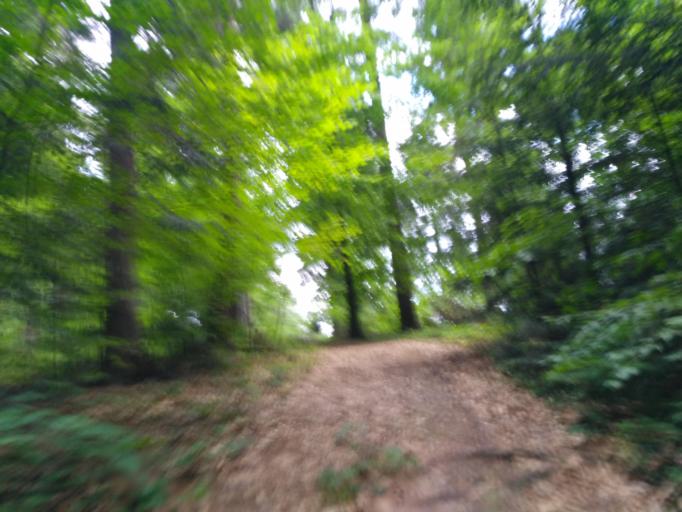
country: PL
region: Subcarpathian Voivodeship
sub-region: Powiat jasielski
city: Brzyska
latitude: 49.8060
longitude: 21.3659
